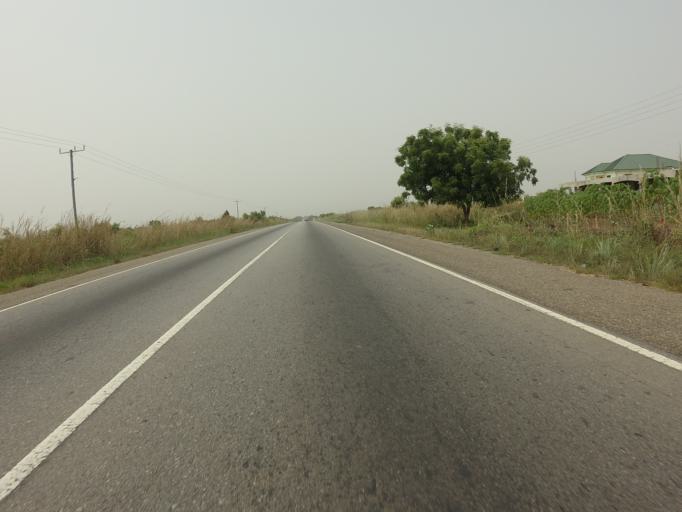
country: GH
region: Volta
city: Anloga
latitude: 5.8896
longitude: 0.4700
